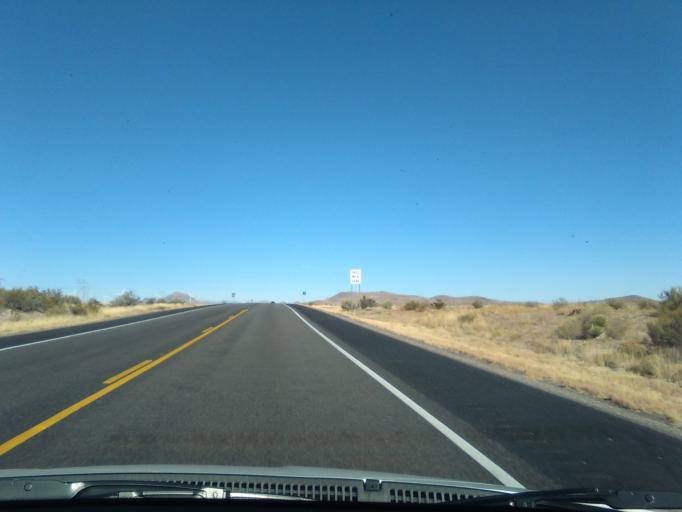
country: US
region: New Mexico
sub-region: Luna County
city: Deming
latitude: 32.4899
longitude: -107.5209
